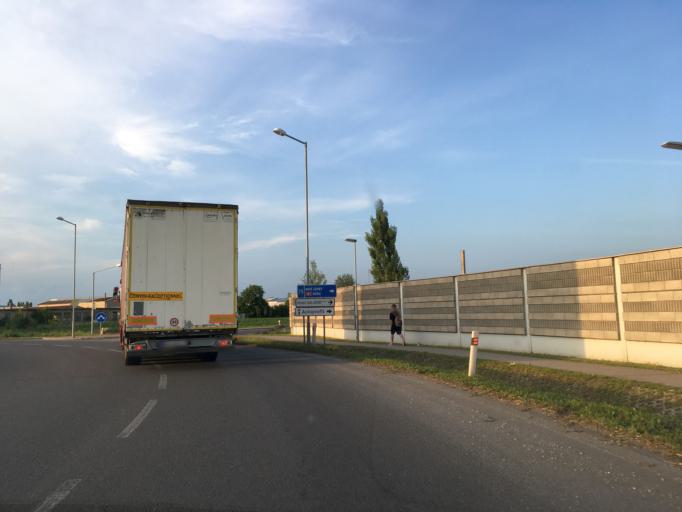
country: SK
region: Trnavsky
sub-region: Okres Galanta
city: Galanta
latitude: 48.1794
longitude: 17.7321
